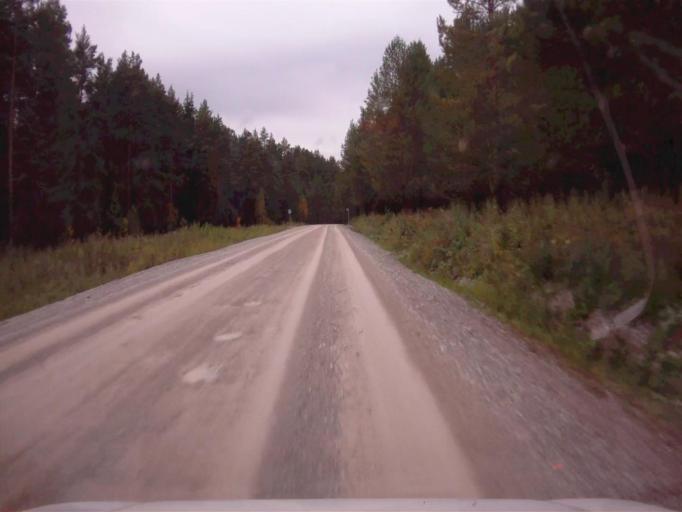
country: RU
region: Chelyabinsk
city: Nyazepetrovsk
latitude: 56.0460
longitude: 59.5208
